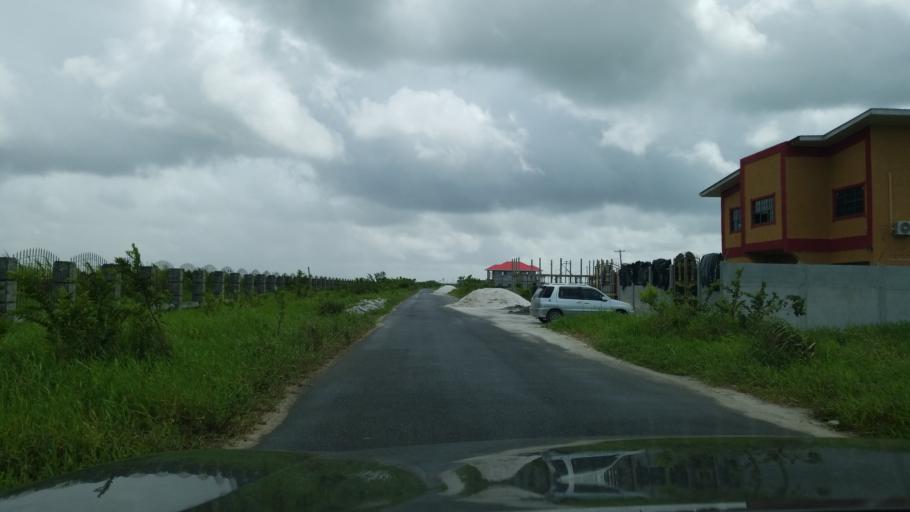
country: GY
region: Demerara-Mahaica
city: Georgetown
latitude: 6.7533
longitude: -58.1624
